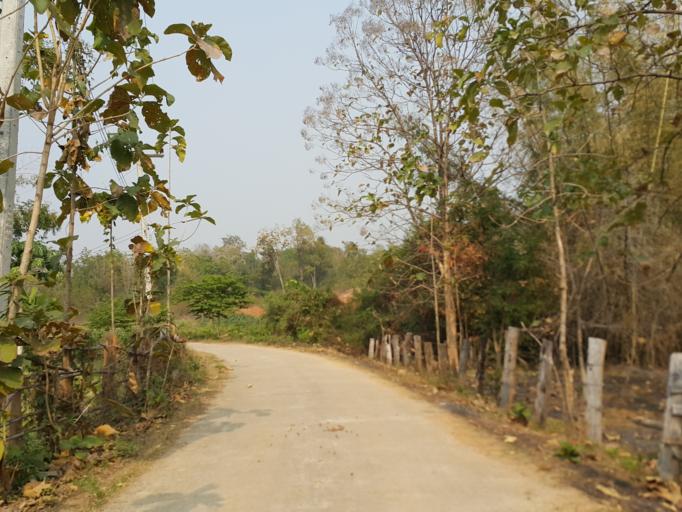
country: TH
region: Lampang
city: Mae Phrik
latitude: 17.4866
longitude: 99.0886
